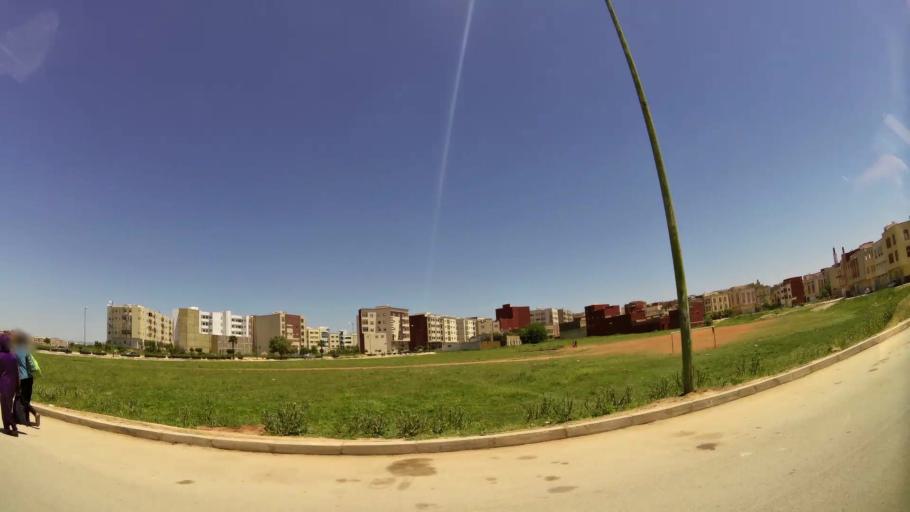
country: MA
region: Meknes-Tafilalet
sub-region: Meknes
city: Meknes
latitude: 33.8583
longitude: -5.5604
